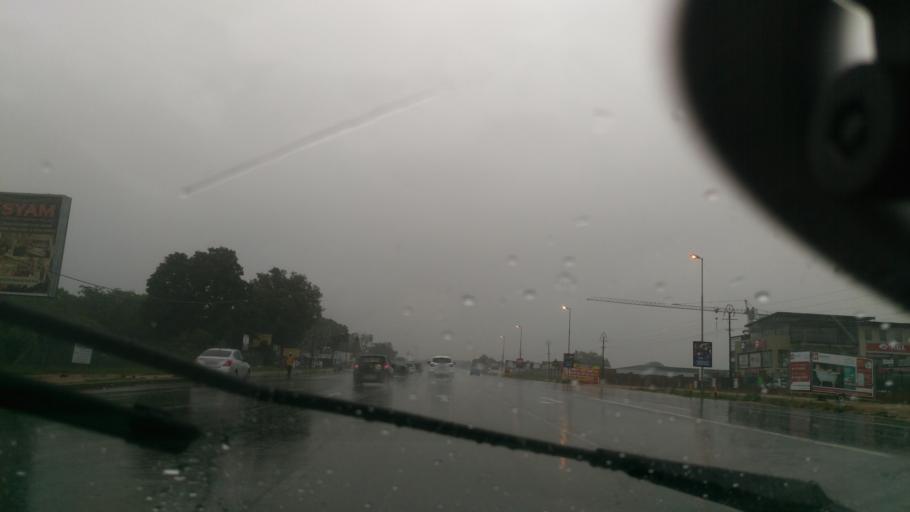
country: ZA
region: Gauteng
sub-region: City of Johannesburg Metropolitan Municipality
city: Diepsloot
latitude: -26.0400
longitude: 27.9588
